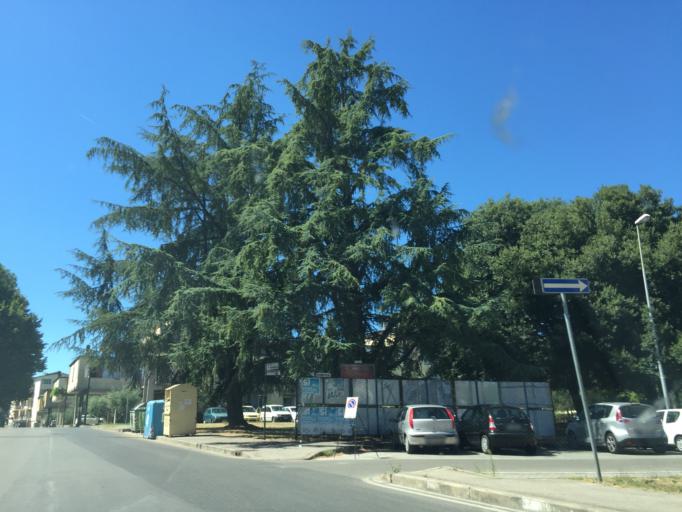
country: IT
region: Tuscany
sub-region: Provincia di Pistoia
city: Pistoia
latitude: 43.9491
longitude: 10.9078
